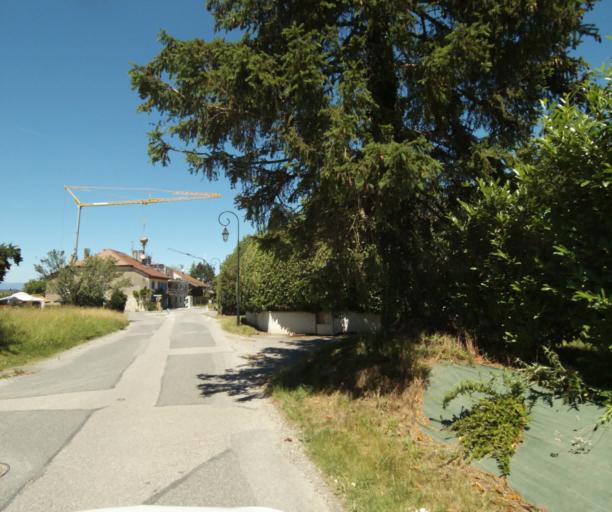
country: FR
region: Rhone-Alpes
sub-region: Departement de la Haute-Savoie
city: Veigy-Foncenex
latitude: 46.2586
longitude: 6.2641
